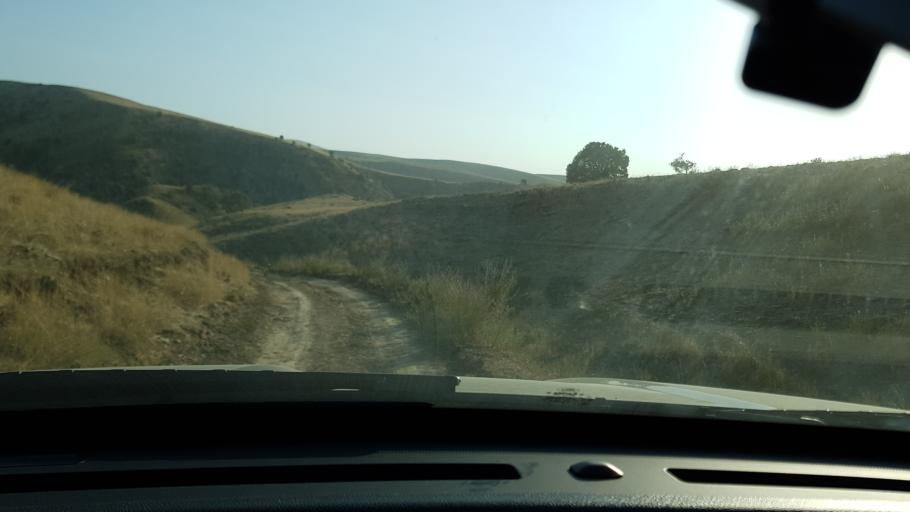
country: TM
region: Ahal
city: Baharly
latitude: 38.4073
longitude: 56.9101
